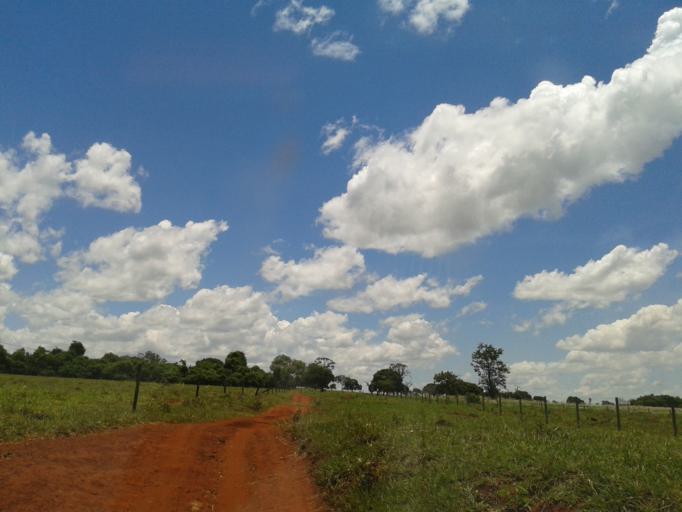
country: BR
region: Minas Gerais
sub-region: Centralina
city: Centralina
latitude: -18.7036
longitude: -49.1766
